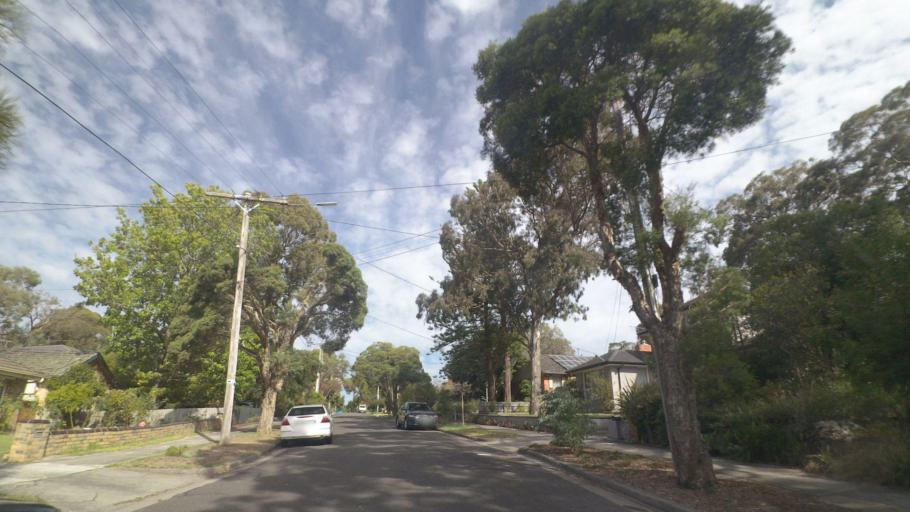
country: AU
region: Victoria
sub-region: Whitehorse
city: Forest Hill
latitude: -37.8346
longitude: 145.1593
